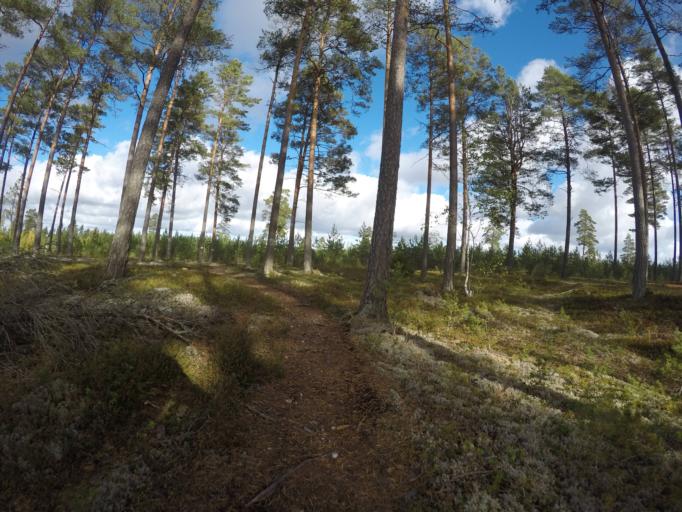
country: SE
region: Vaestmanland
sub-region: Kungsors Kommun
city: Kungsoer
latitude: 59.3095
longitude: 16.1100
